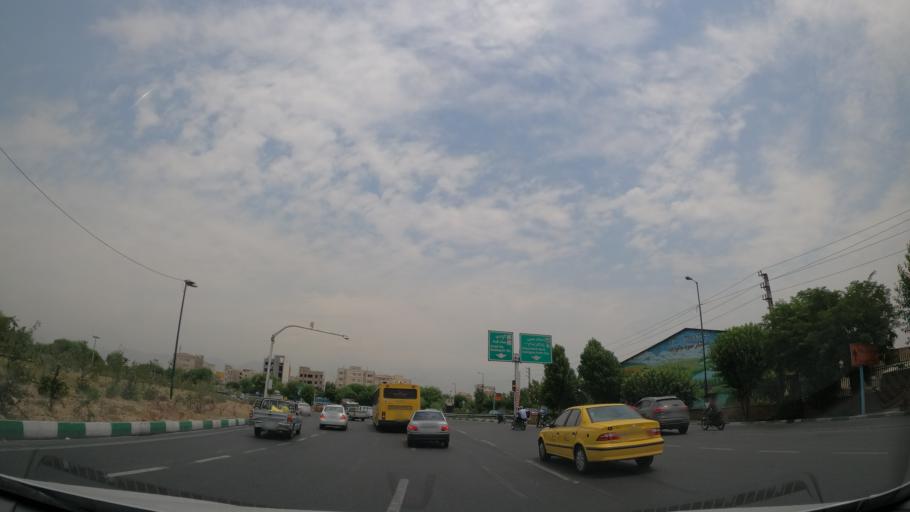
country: IR
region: Tehran
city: Tehran
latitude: 35.6825
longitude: 51.3432
